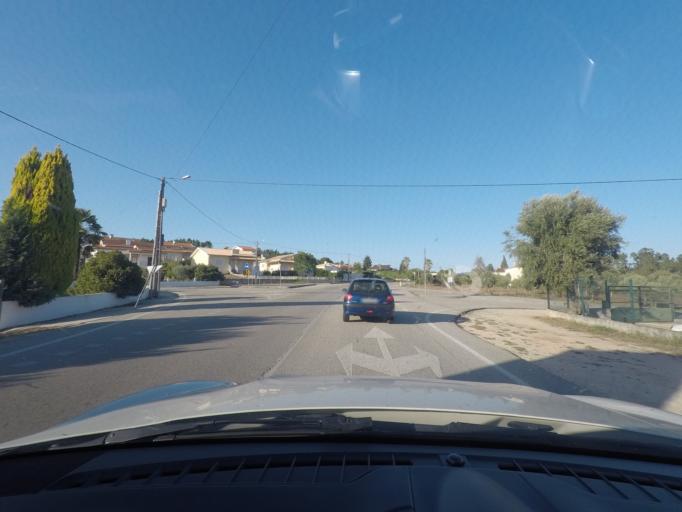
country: PT
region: Coimbra
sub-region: Vila Nova de Poiares
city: Poiares
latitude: 40.1799
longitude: -8.2643
